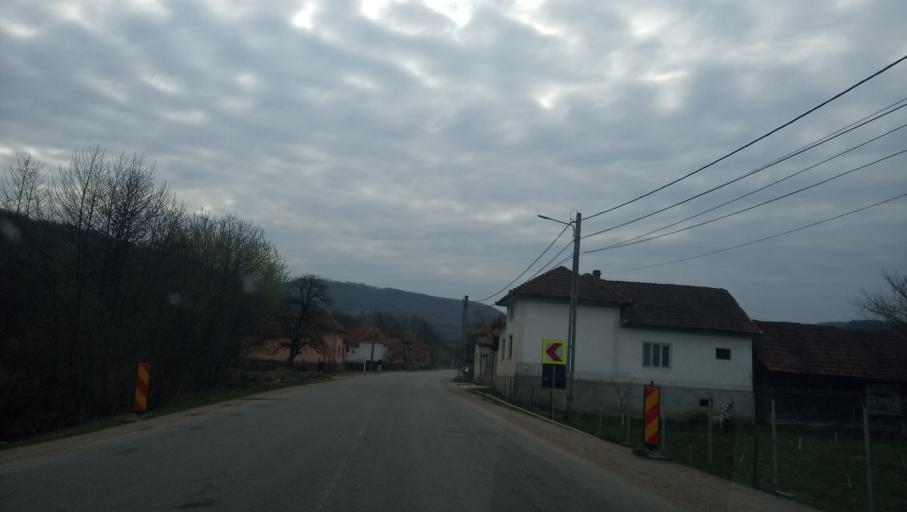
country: RO
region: Bihor
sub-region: Comuna Cristioru de Jos
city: Cristioru de Jos
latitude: 46.4245
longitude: 22.5293
